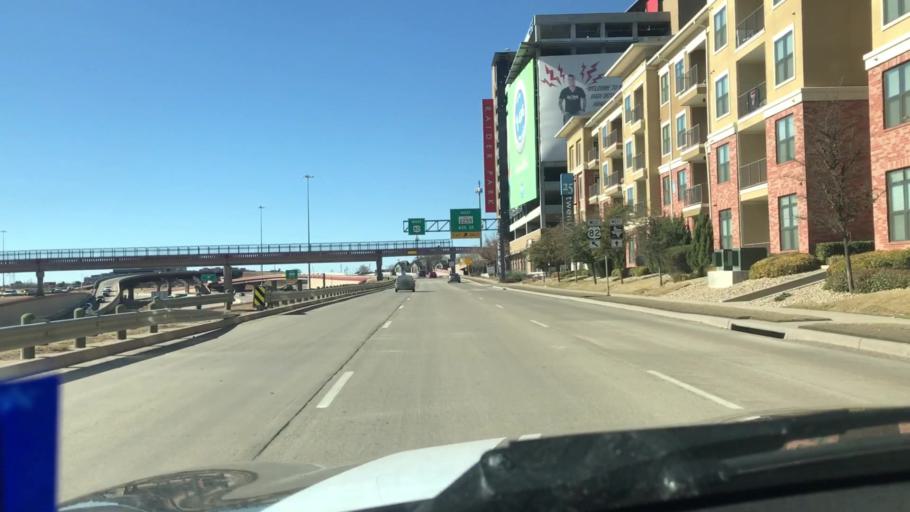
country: US
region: Texas
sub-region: Lubbock County
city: Lubbock
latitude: 33.5931
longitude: -101.8725
